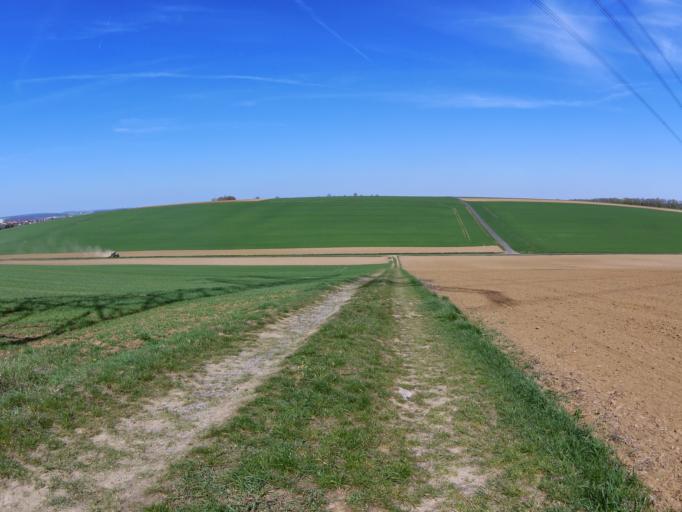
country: DE
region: Bavaria
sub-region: Regierungsbezirk Unterfranken
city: Rottendorf
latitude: 49.7884
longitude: 10.0528
